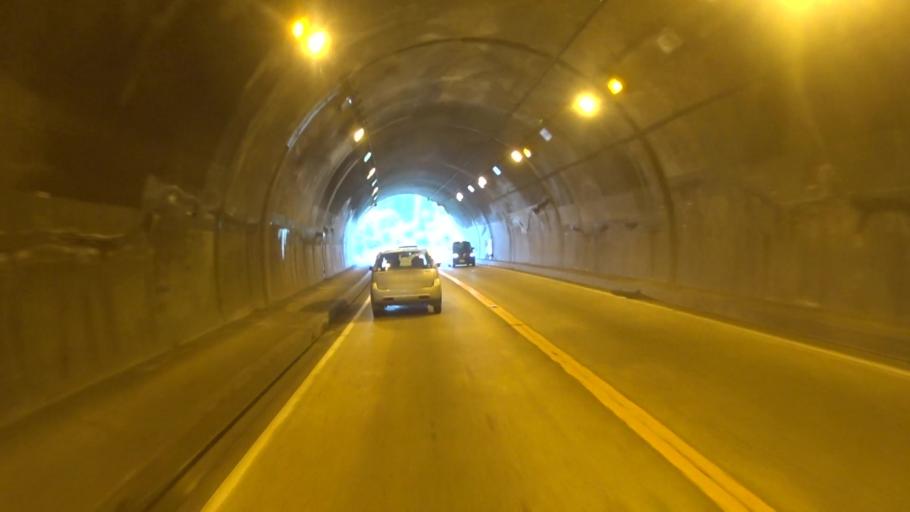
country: JP
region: Kyoto
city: Miyazu
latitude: 35.5504
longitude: 135.1724
